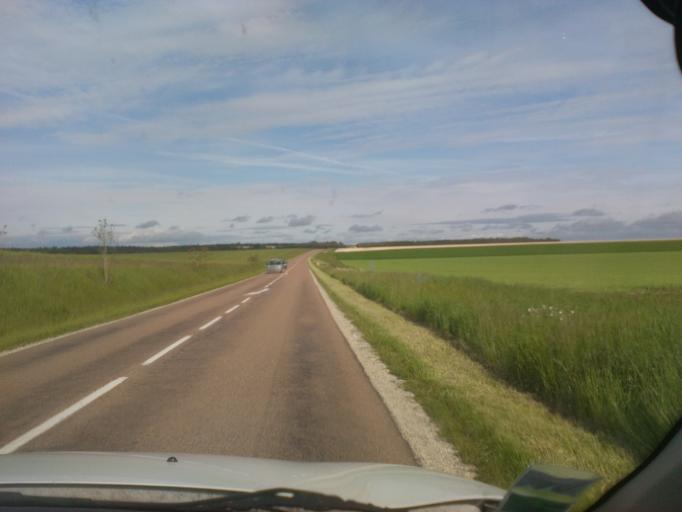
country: FR
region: Champagne-Ardenne
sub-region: Departement de l'Aube
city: Payns
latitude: 48.3736
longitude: 3.8885
